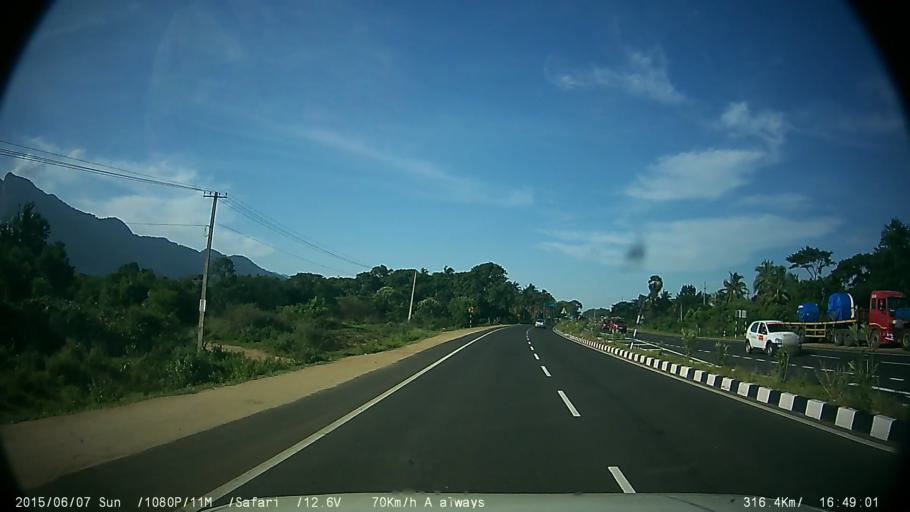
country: IN
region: Kerala
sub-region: Palakkad district
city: Chittur
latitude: 10.8060
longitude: 76.7892
